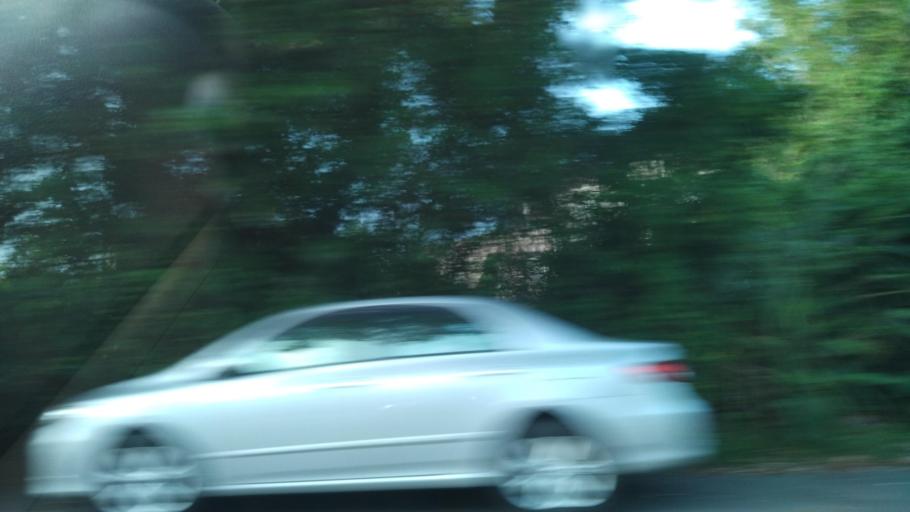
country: TW
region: Taiwan
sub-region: Keelung
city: Keelung
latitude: 25.2175
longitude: 121.6386
